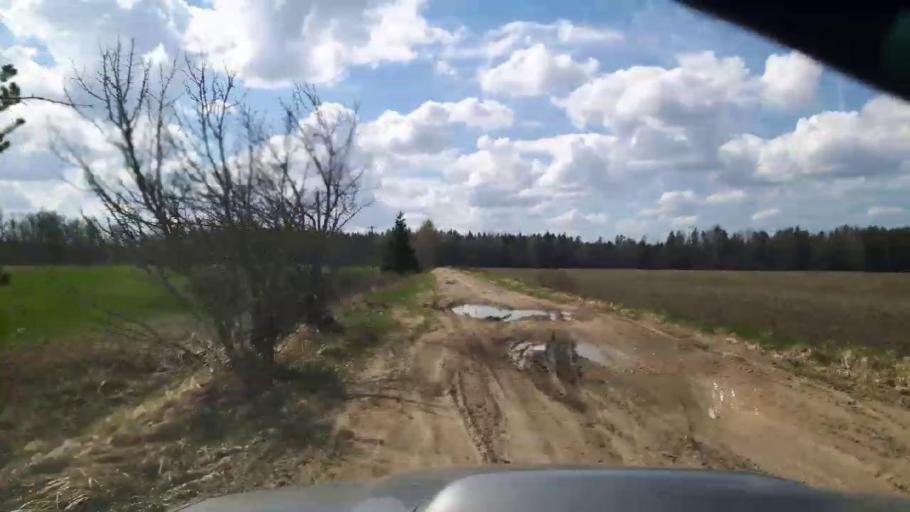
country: EE
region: Paernumaa
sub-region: Vaendra vald (alev)
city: Vandra
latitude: 58.5394
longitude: 25.0682
